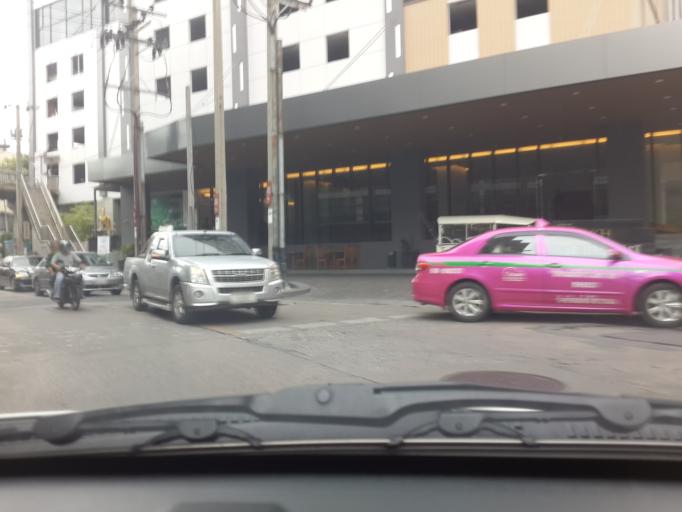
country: TH
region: Bangkok
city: Khlong Toei
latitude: 13.7209
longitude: 100.5657
